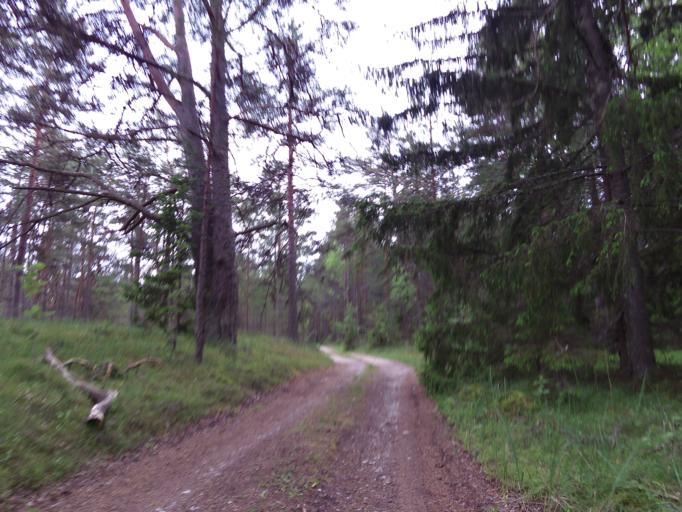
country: EE
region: Harju
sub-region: Paldiski linn
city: Paldiski
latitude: 59.2461
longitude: 23.7477
